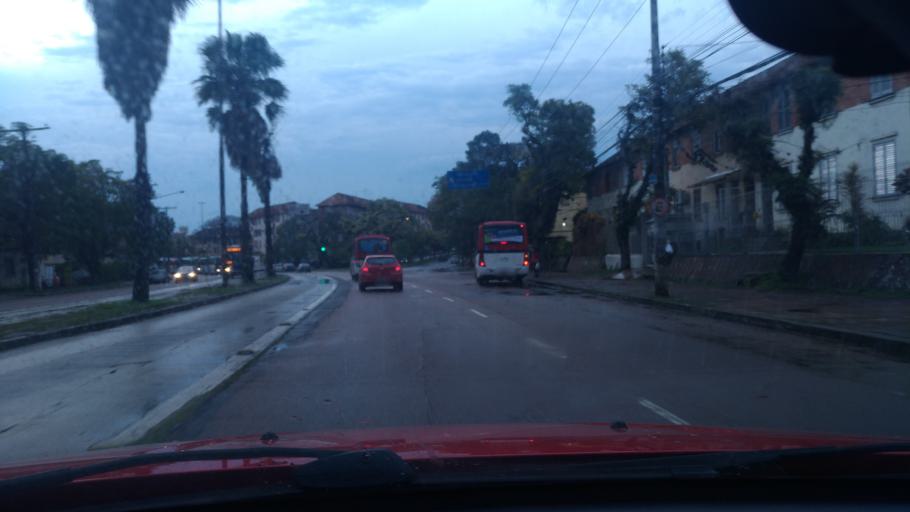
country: BR
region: Rio Grande do Sul
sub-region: Porto Alegre
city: Porto Alegre
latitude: -30.0107
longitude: -51.1761
